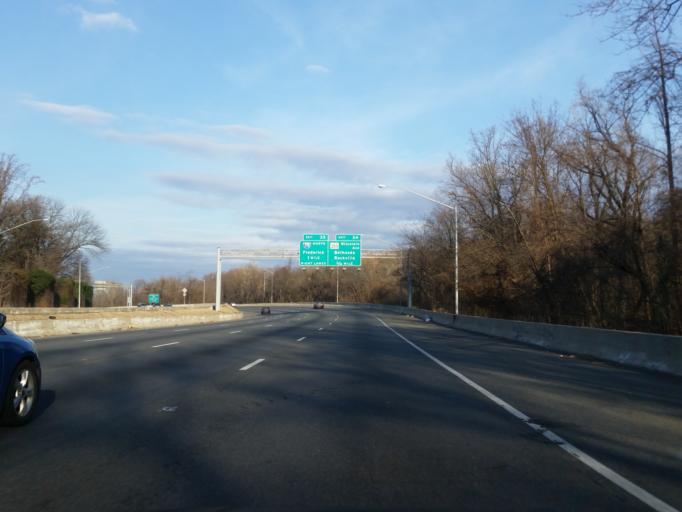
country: US
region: Maryland
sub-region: Montgomery County
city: South Kensington
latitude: 39.0090
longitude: -77.0880
